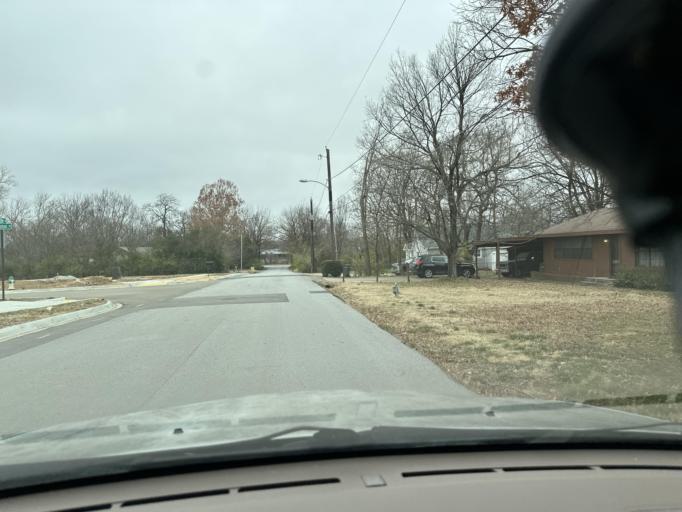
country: US
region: Arkansas
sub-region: Washington County
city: Fayetteville
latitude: 36.0905
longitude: -94.1601
